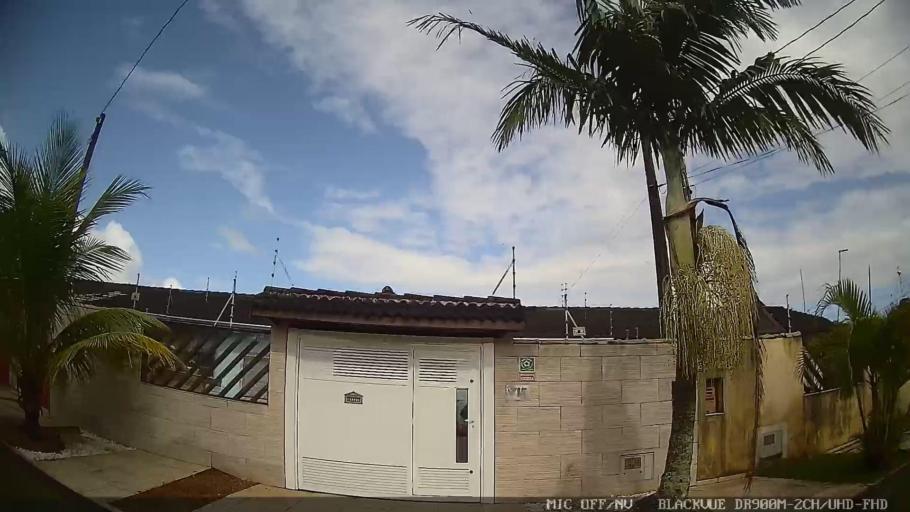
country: BR
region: Sao Paulo
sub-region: Itanhaem
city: Itanhaem
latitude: -24.2072
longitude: -46.8430
